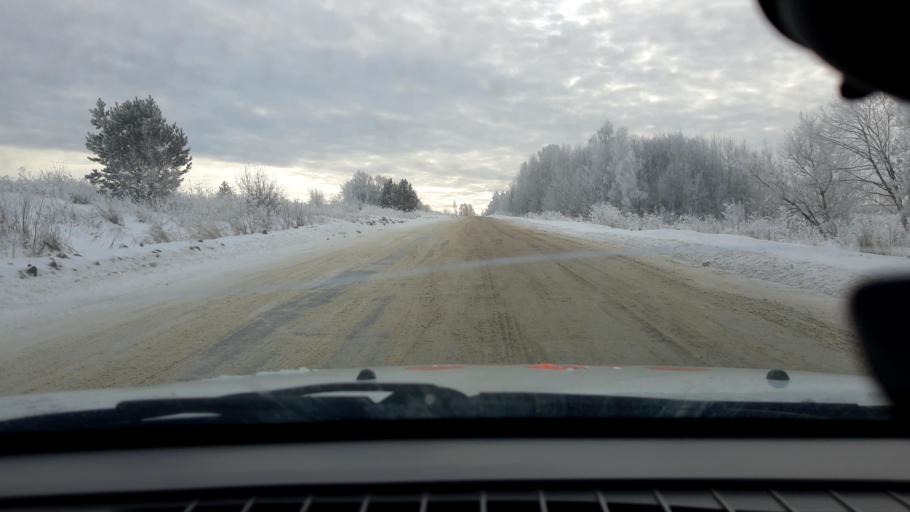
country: RU
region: Nizjnij Novgorod
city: Bogorodsk
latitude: 56.0783
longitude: 43.5756
